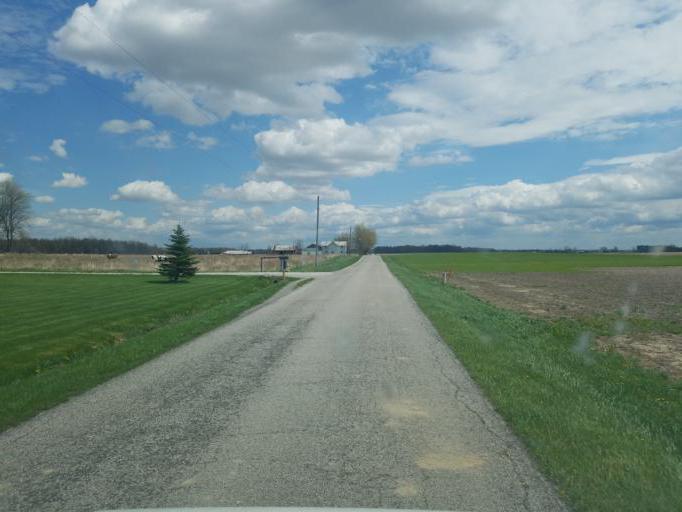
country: US
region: Ohio
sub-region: Crawford County
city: Bucyrus
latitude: 40.9067
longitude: -82.9376
